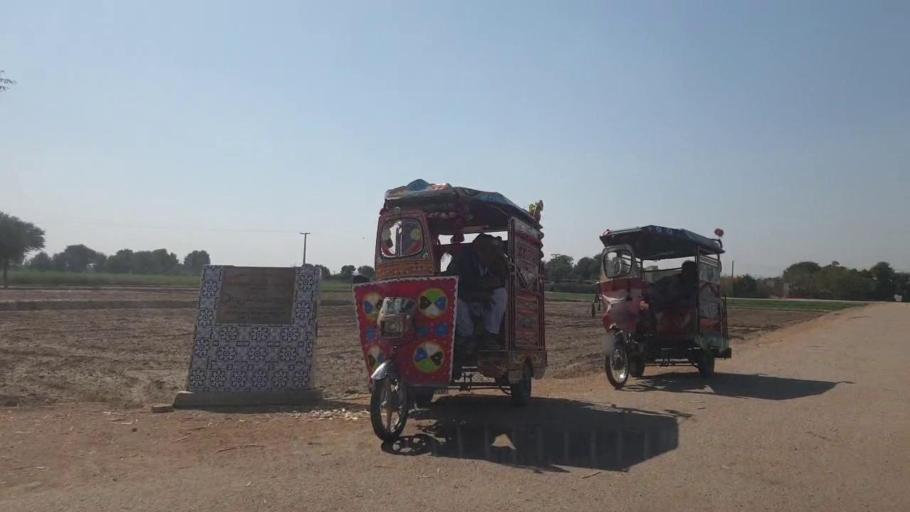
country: PK
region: Sindh
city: Chambar
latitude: 25.2908
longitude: 68.6612
